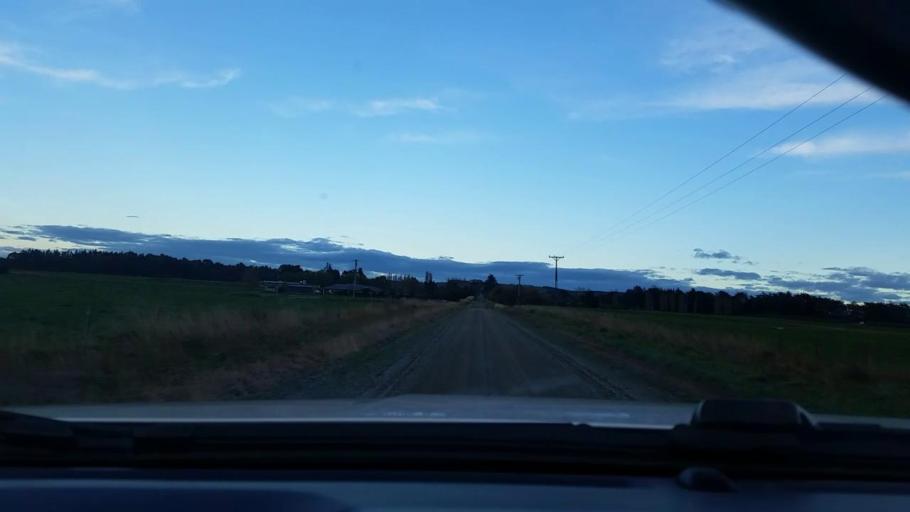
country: NZ
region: Southland
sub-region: Southland District
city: Winton
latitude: -46.1016
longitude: 168.4689
